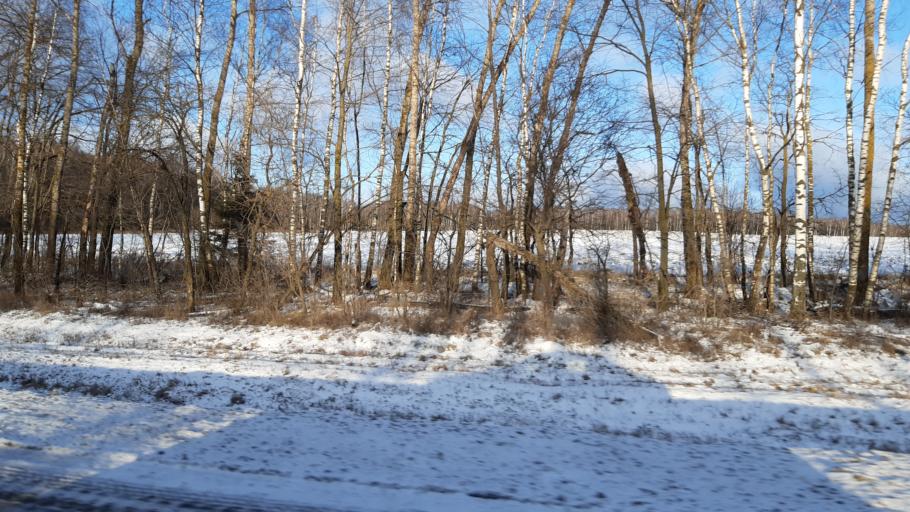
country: RU
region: Vladimir
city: Arsaki
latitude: 56.2904
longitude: 38.3835
